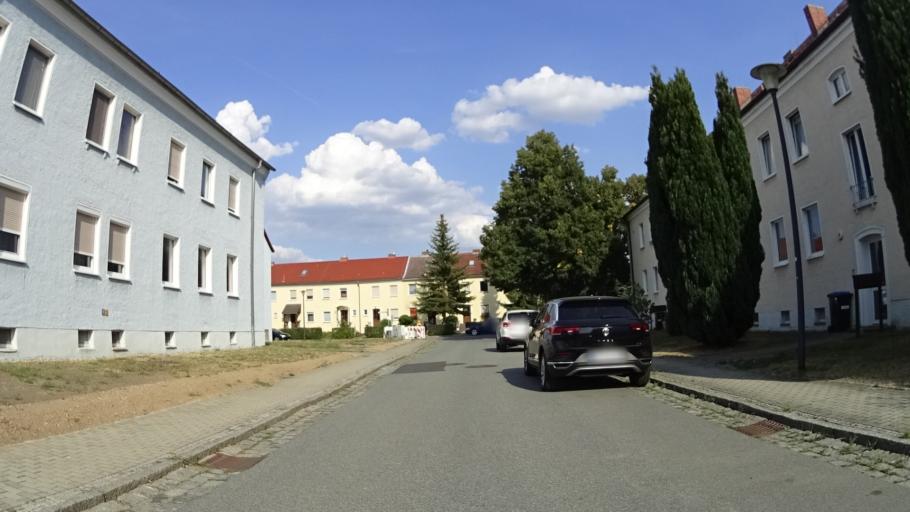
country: DE
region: Saxony
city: Ostritz
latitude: 51.0694
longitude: 14.9638
